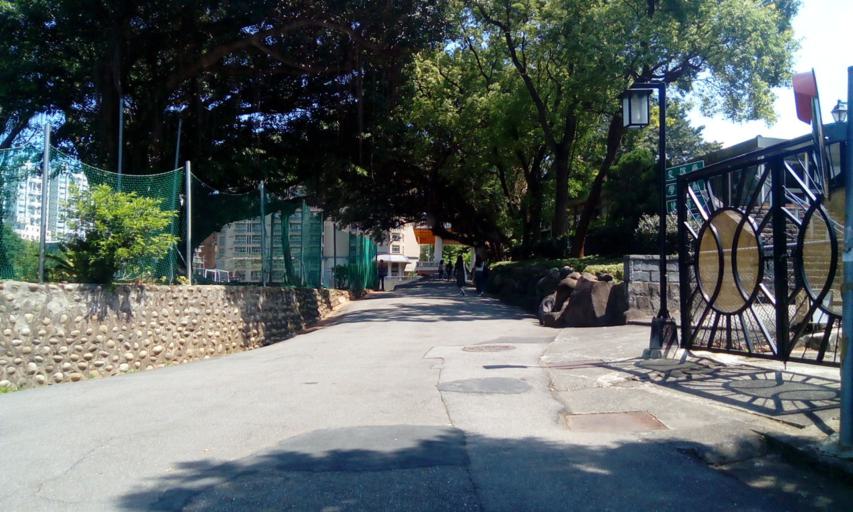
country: TW
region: Taipei
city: Taipei
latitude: 25.1766
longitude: 121.4353
